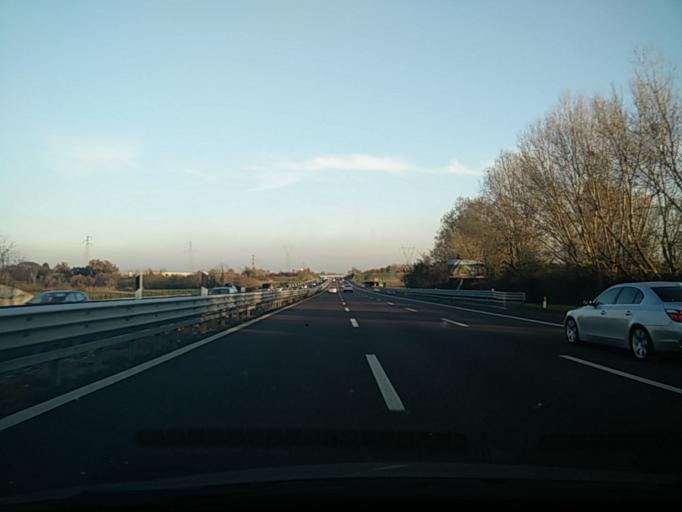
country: IT
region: Veneto
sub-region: Provincia di Verona
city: Cavalcaselle
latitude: 45.4281
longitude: 10.7419
